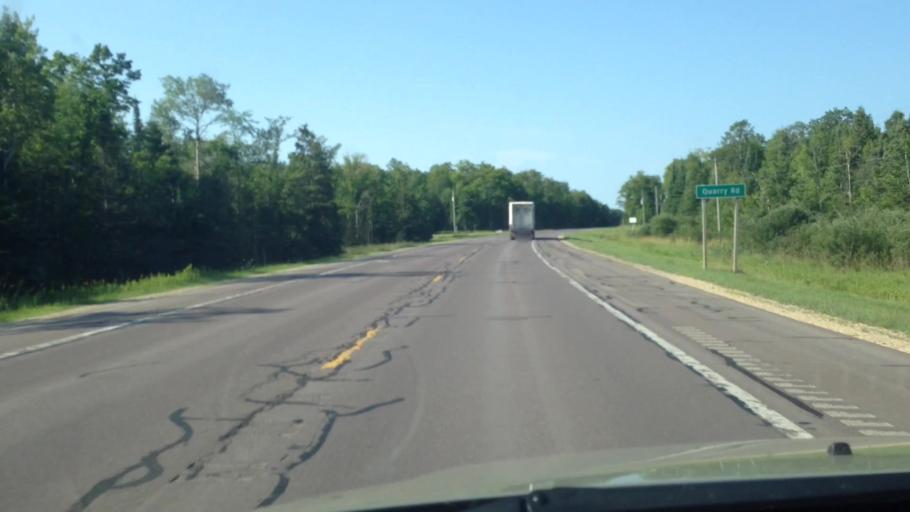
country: US
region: Michigan
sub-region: Schoolcraft County
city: Manistique
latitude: 46.0587
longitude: -85.9596
